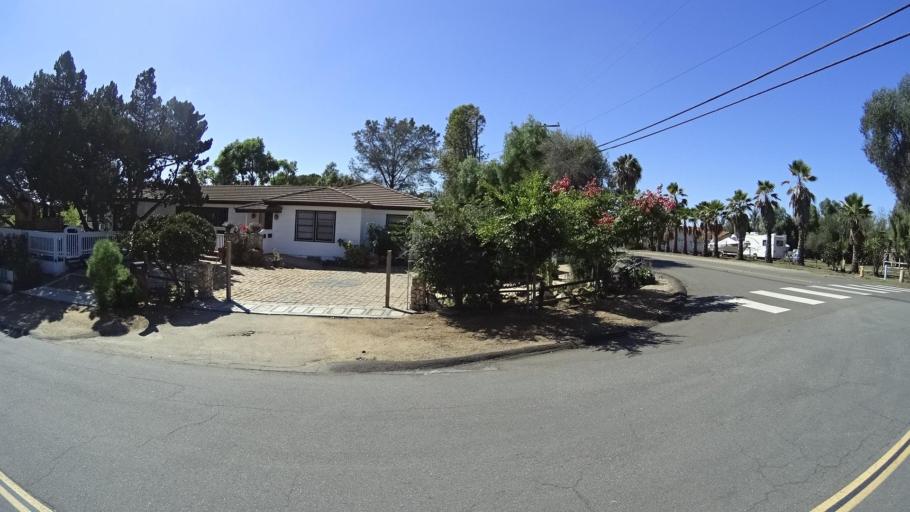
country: US
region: California
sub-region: San Diego County
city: Bonita
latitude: 32.6560
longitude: -117.0538
